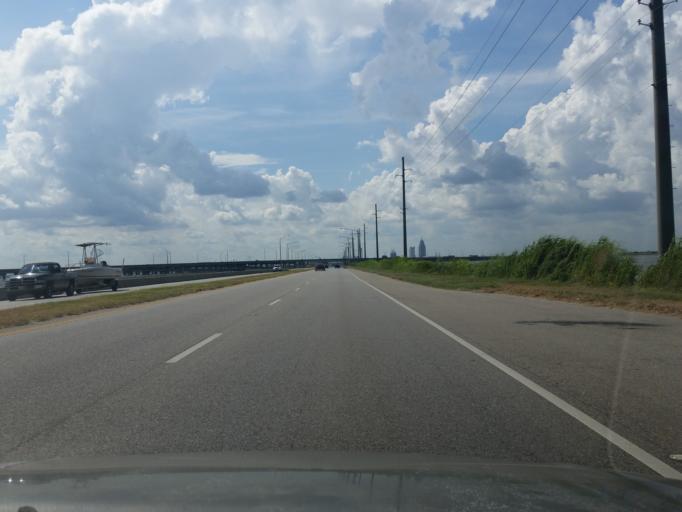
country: US
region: Alabama
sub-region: Baldwin County
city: Spanish Fort
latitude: 30.6767
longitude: -87.9779
